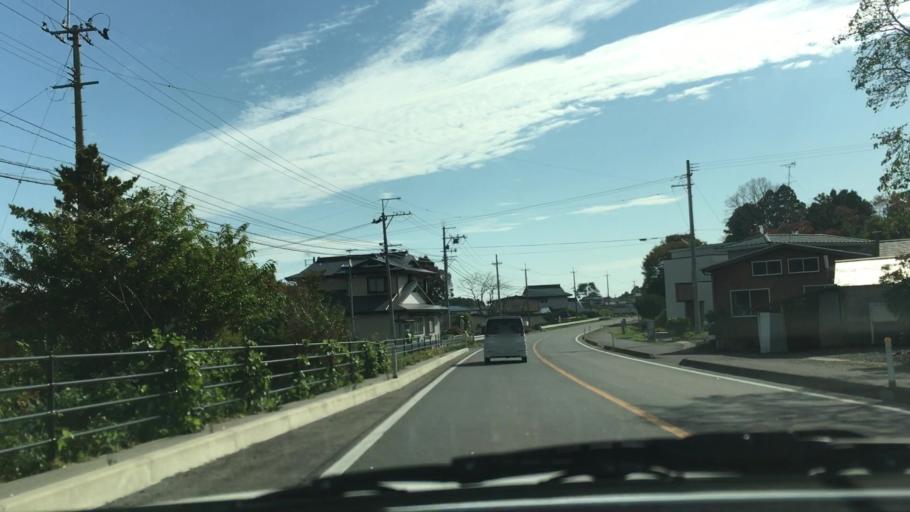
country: JP
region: Aomori
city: Hachinohe
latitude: 40.4263
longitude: 141.6953
